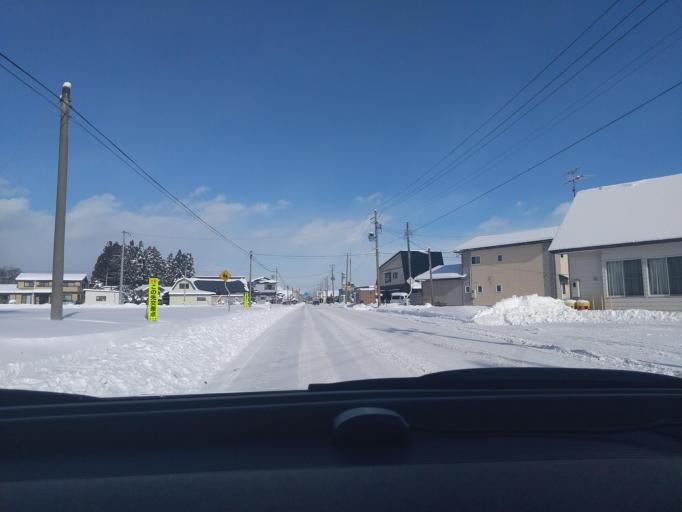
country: JP
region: Iwate
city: Hanamaki
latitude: 39.3858
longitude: 141.0555
